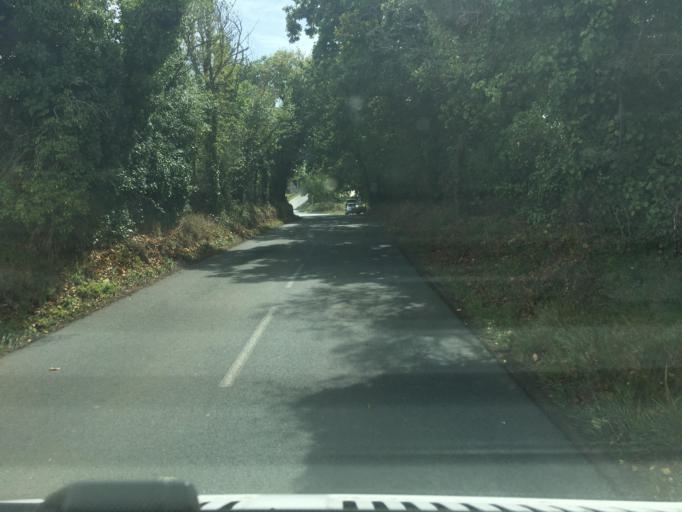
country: FR
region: Brittany
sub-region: Departement du Finistere
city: Loctudy
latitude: 47.8231
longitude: -4.1744
